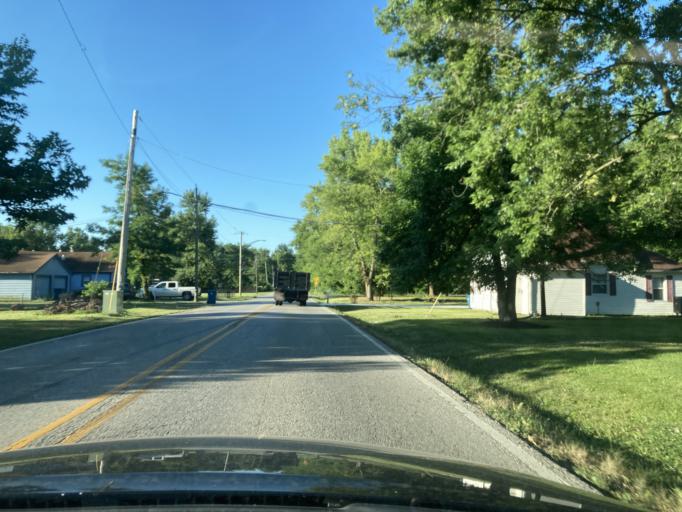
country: US
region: Indiana
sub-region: Marion County
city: Meridian Hills
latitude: 39.8648
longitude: -86.2122
